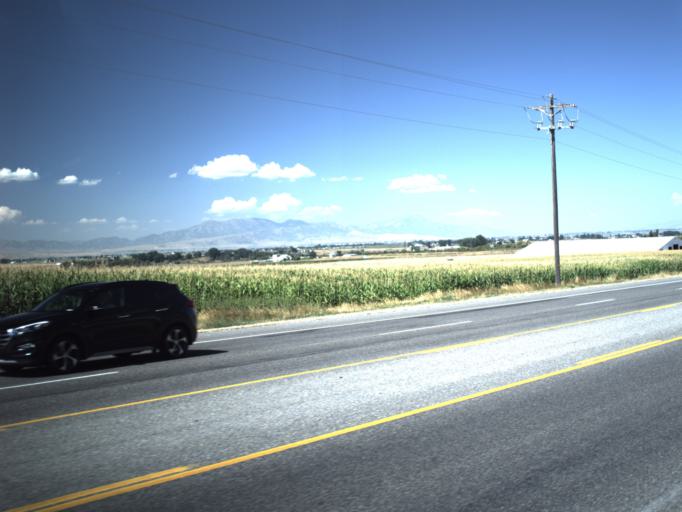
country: US
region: Utah
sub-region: Cache County
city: Richmond
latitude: 41.9266
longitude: -111.8141
